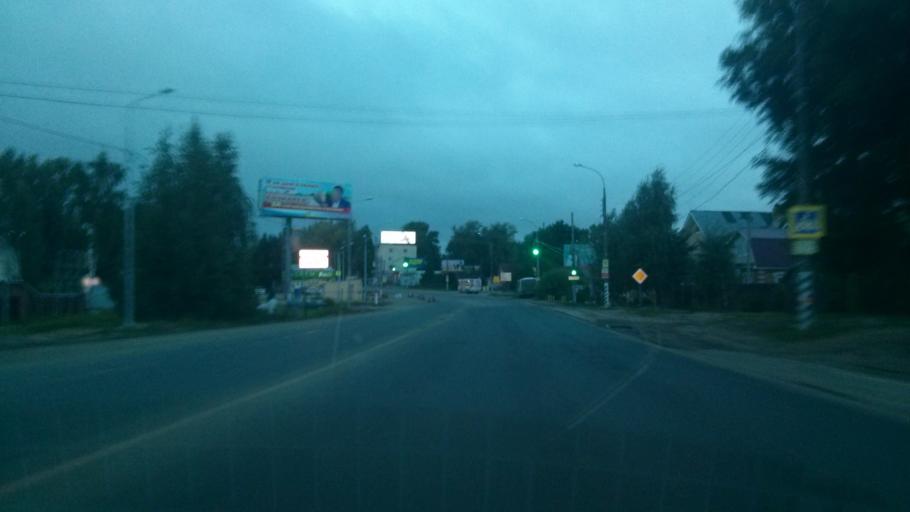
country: RU
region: Nizjnij Novgorod
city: Afonino
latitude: 56.2654
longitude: 44.0944
